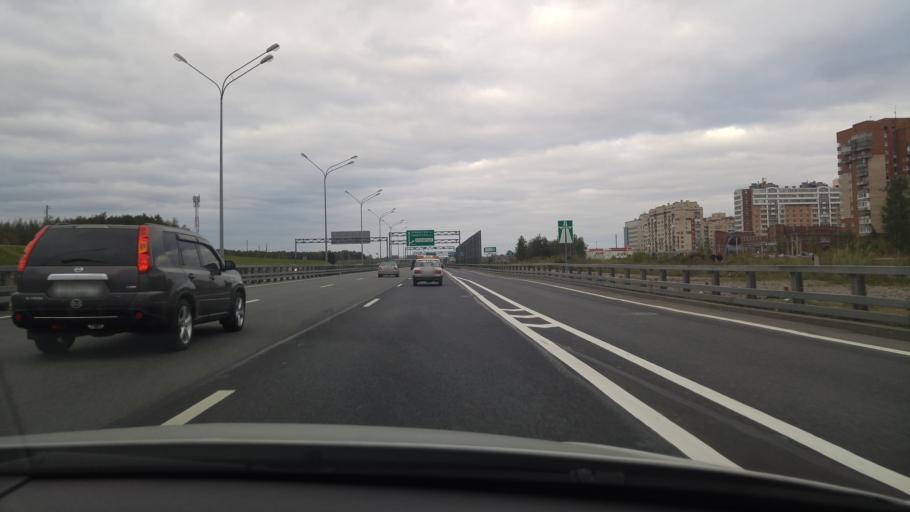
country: RU
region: St.-Petersburg
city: Kronshtadt
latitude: 60.0085
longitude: 29.7125
